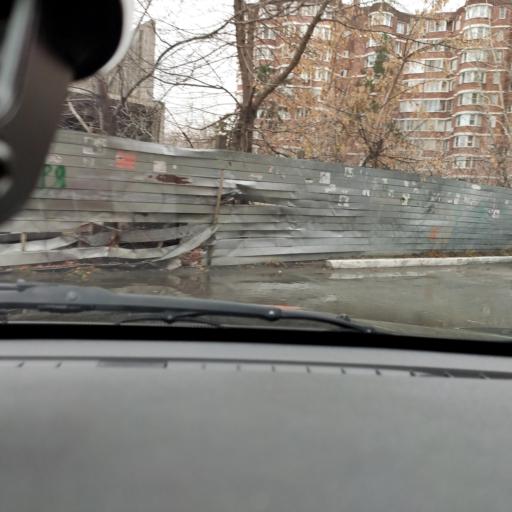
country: RU
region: Samara
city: Tol'yatti
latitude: 53.5374
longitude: 49.3627
